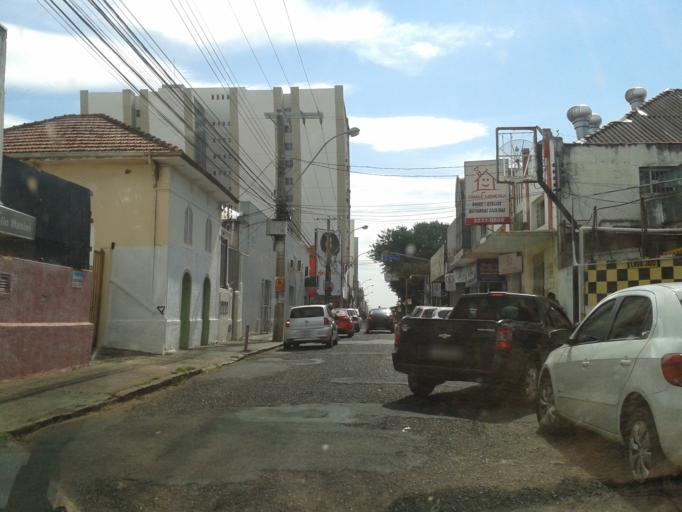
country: BR
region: Minas Gerais
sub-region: Uberlandia
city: Uberlandia
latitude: -18.9171
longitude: -48.2743
